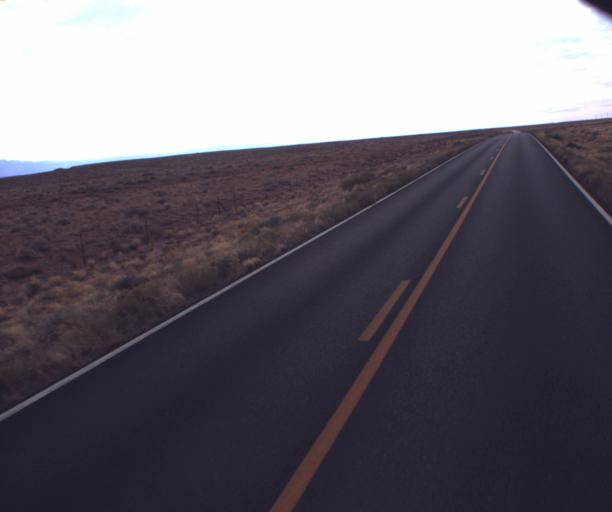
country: US
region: Arizona
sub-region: Apache County
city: Many Farms
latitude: 36.5699
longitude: -109.5469
